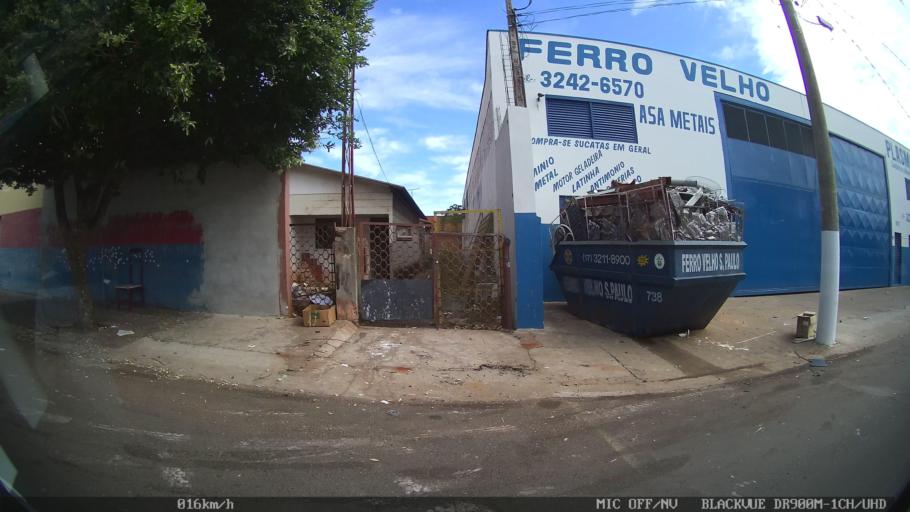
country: BR
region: Sao Paulo
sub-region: Bady Bassitt
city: Bady Bassitt
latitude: -20.8233
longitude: -49.5236
